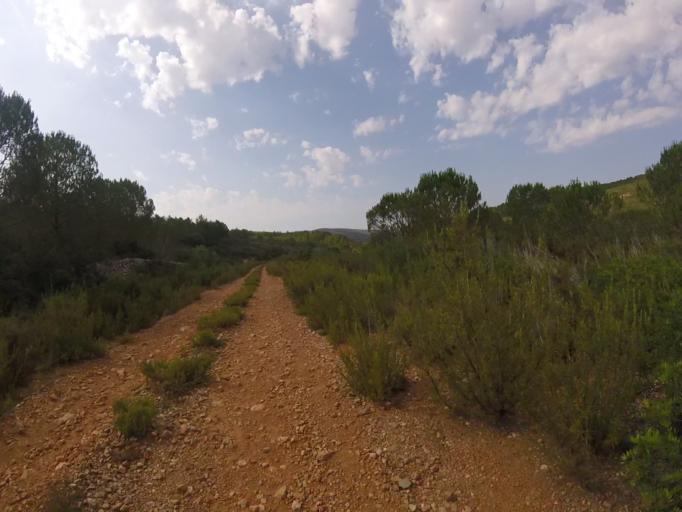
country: ES
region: Valencia
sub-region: Provincia de Castello
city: Alcala de Xivert
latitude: 40.3471
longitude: 0.1983
